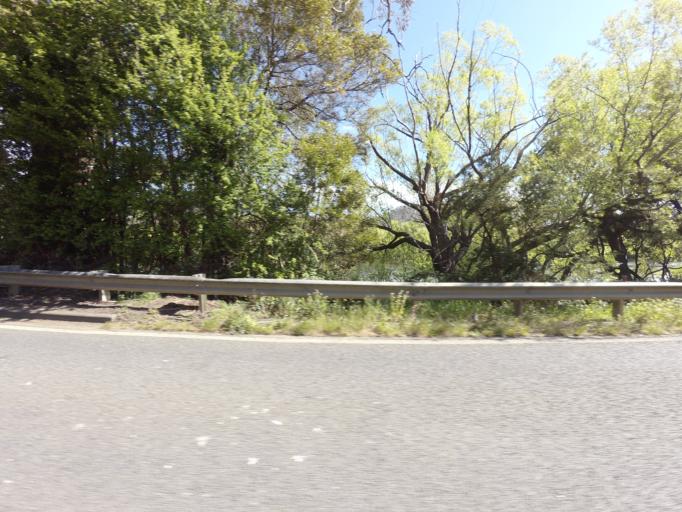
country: AU
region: Tasmania
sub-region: Derwent Valley
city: New Norfolk
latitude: -42.7681
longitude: 147.0262
